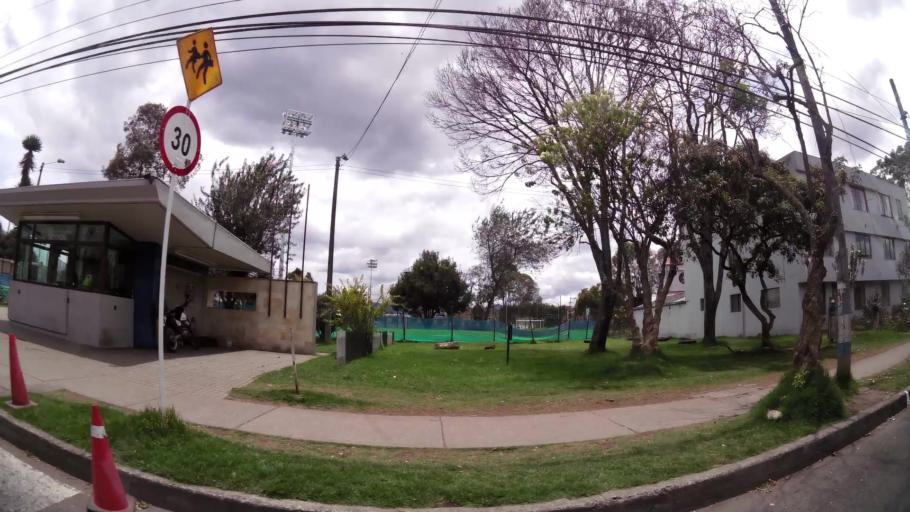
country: CO
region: Cundinamarca
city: Funza
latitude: 4.7170
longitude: -74.1231
